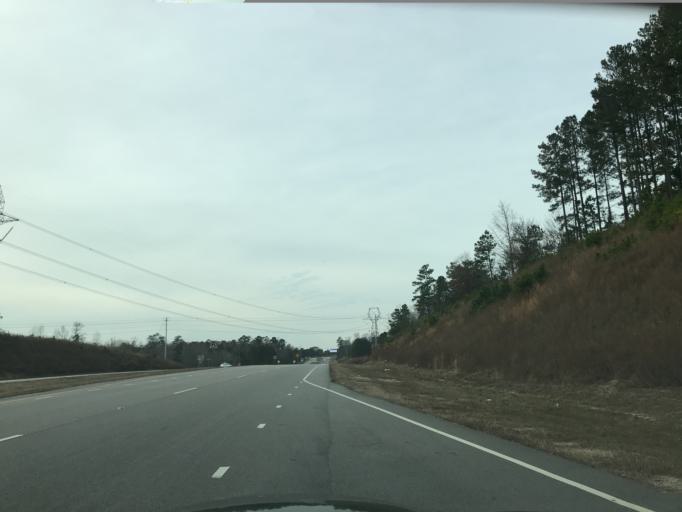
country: US
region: North Carolina
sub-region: Wake County
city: Rolesville
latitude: 35.8999
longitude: -78.4768
